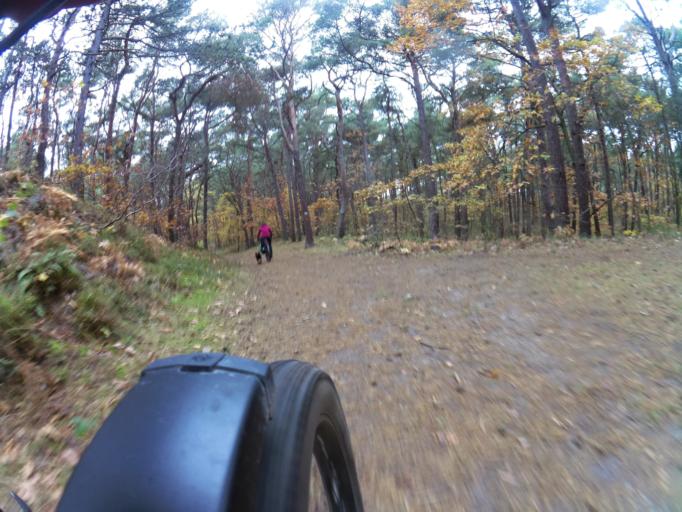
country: PL
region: Pomeranian Voivodeship
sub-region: Powiat pucki
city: Jastarnia
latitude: 54.6940
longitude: 18.6934
